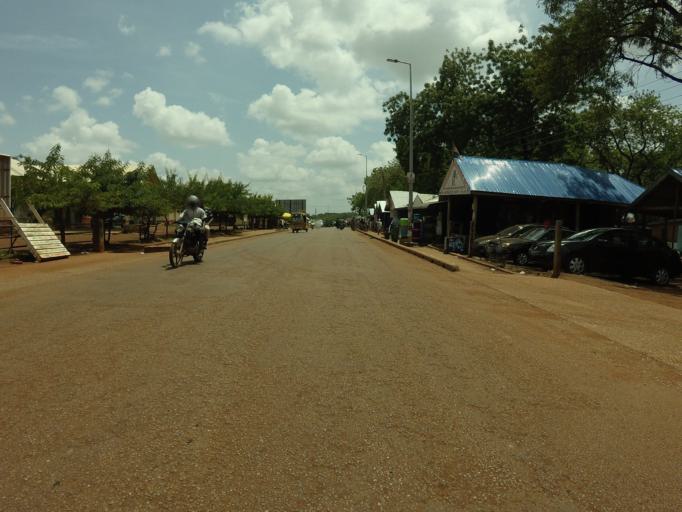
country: GH
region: Northern
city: Tamale
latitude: 9.4018
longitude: -0.8501
